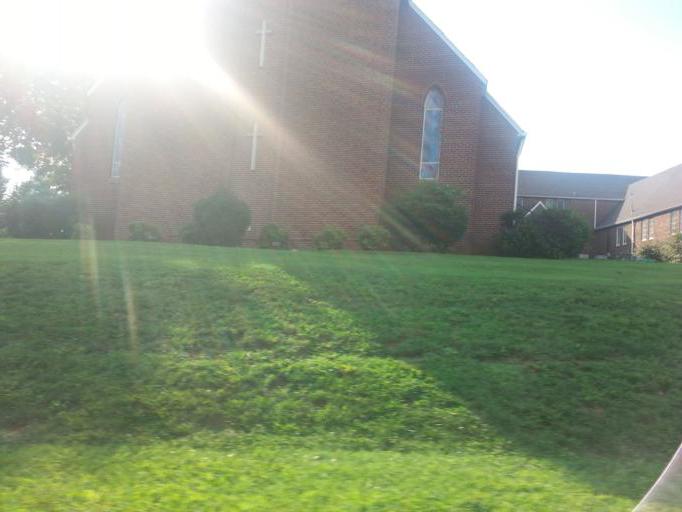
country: US
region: Tennessee
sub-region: Blount County
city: Eagleton Village
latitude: 35.7823
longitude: -83.9487
